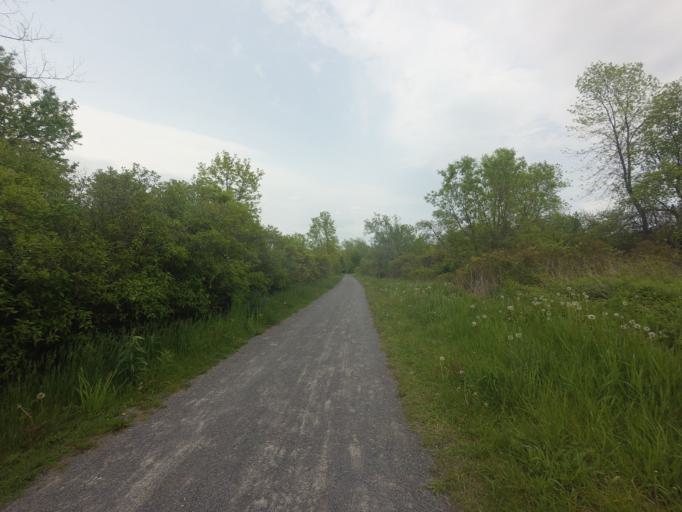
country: CA
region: Ontario
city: Kingston
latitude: 44.2875
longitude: -76.5604
